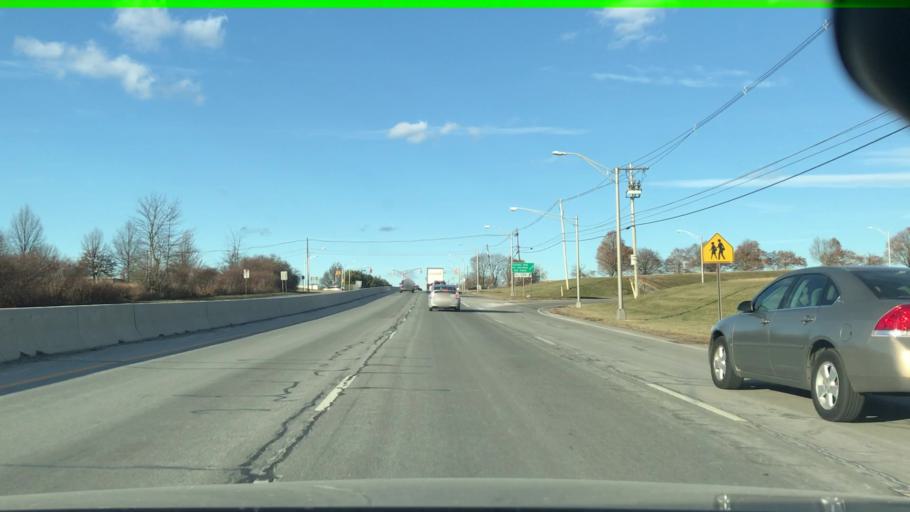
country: US
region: New Jersey
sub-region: Hunterdon County
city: Annandale
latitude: 40.6237
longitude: -74.8806
